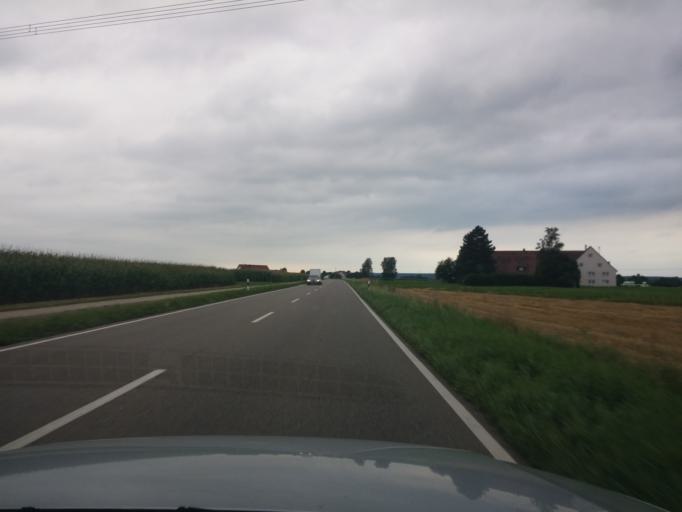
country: DE
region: Bavaria
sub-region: Swabia
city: Buxheim
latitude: 47.9667
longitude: 10.1401
